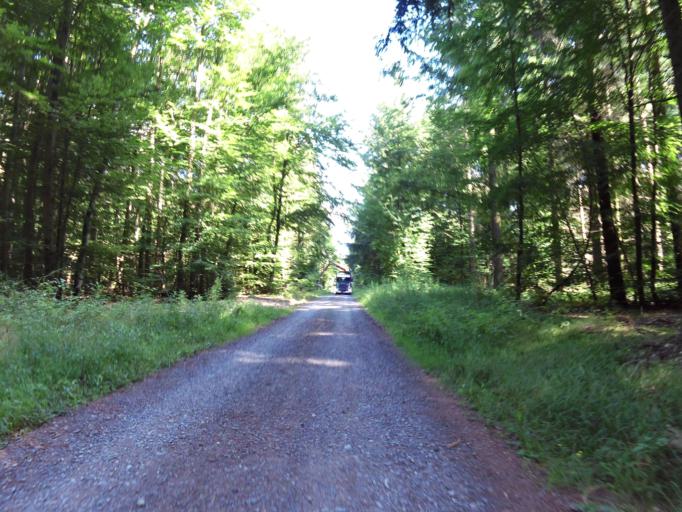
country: DE
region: Rheinland-Pfalz
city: Breunigweiler
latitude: 49.5350
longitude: 7.9630
